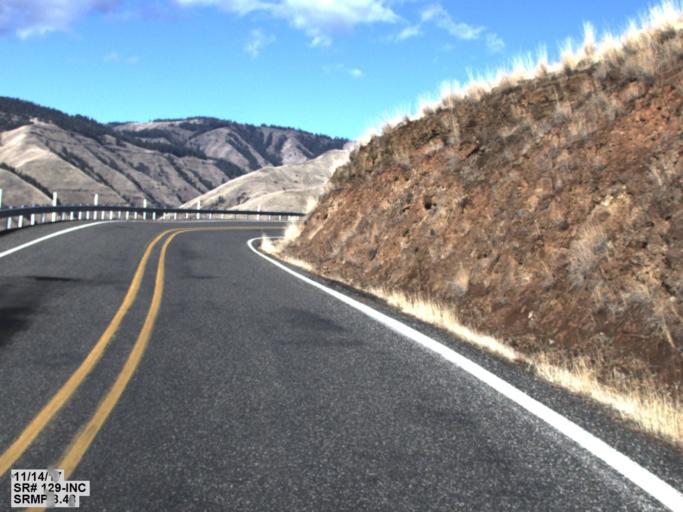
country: US
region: Washington
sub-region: Asotin County
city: Asotin
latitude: 46.0578
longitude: -117.2318
